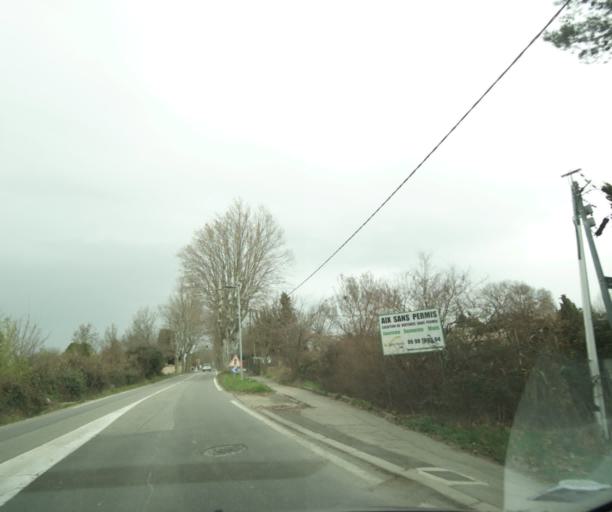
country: FR
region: Provence-Alpes-Cote d'Azur
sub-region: Departement des Bouches-du-Rhone
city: Aix-en-Provence
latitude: 43.5580
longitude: 5.4608
